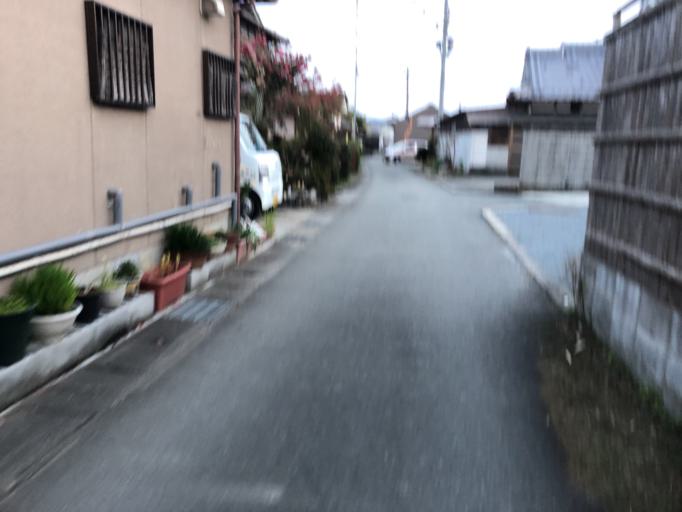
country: JP
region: Kyoto
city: Kameoka
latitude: 35.0579
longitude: 135.5617
